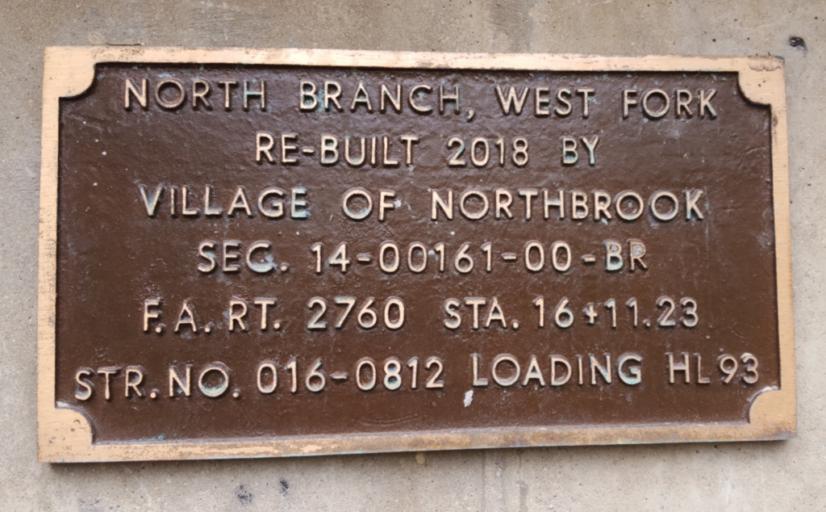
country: US
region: Illinois
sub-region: Cook County
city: Northbrook
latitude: 42.1295
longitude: -87.8257
